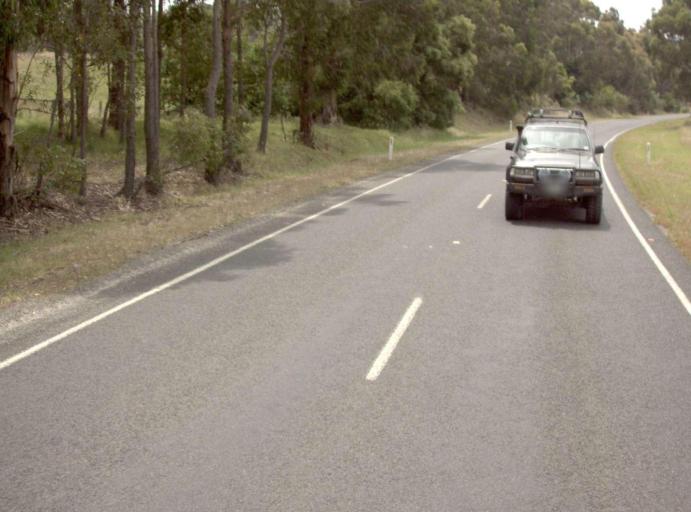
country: AU
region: Victoria
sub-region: Latrobe
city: Traralgon
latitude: -38.4643
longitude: 146.7192
